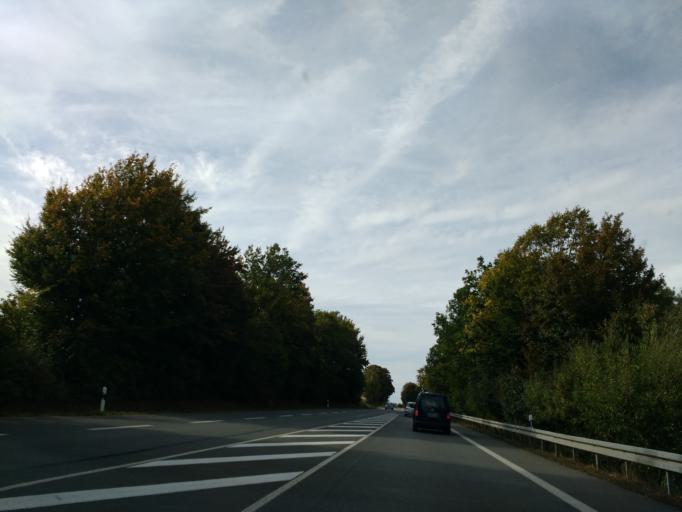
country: DE
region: North Rhine-Westphalia
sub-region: Regierungsbezirk Detmold
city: Nieheim
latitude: 51.8019
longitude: 9.1331
